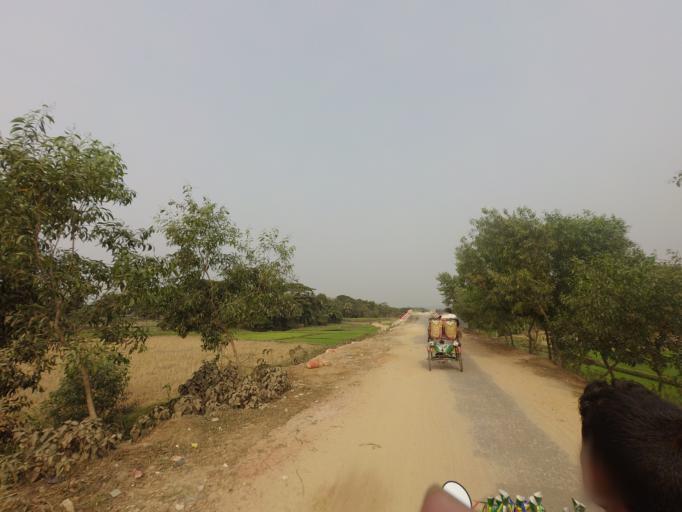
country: BD
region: Dhaka
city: Netrakona
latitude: 25.1489
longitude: 90.6593
